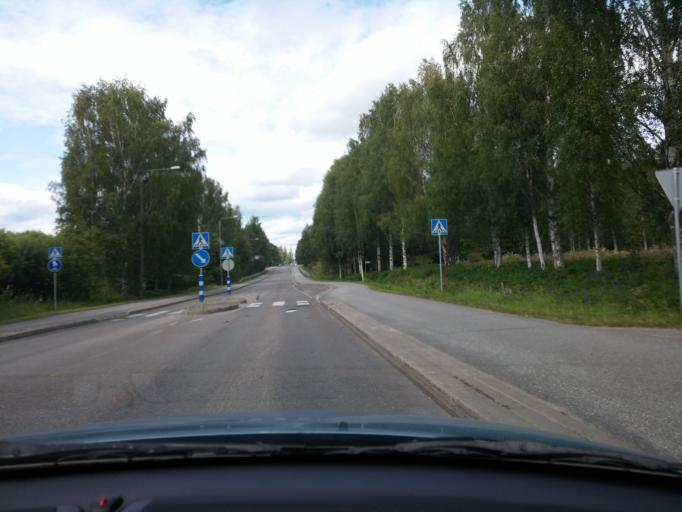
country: FI
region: Central Finland
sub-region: Saarijaervi-Viitasaari
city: Saarijaervi
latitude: 62.7079
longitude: 25.2242
